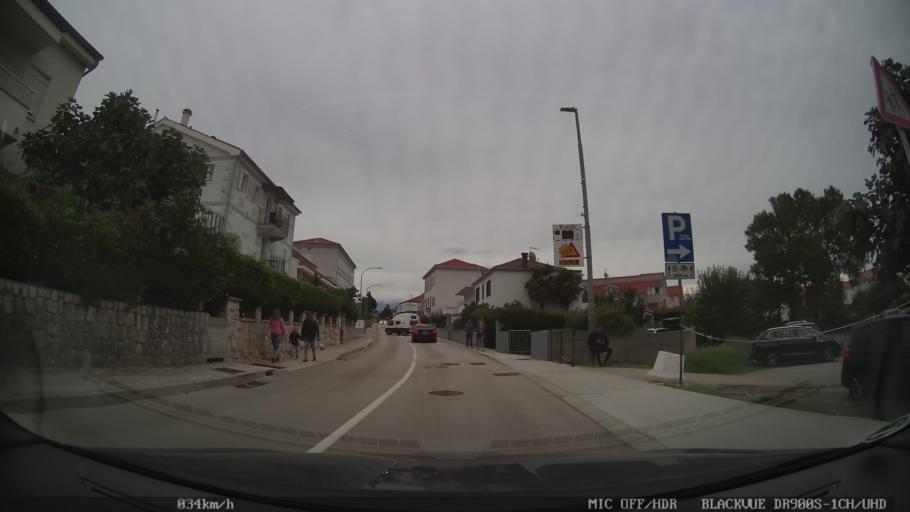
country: HR
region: Primorsko-Goranska
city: Punat
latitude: 44.9703
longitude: 14.7501
